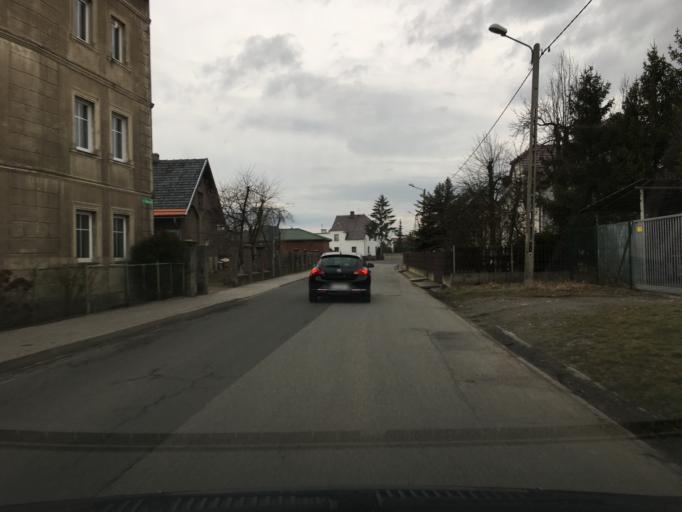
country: PL
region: Opole Voivodeship
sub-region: Powiat kedzierzynsko-kozielski
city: Kozle
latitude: 50.3520
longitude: 18.1337
